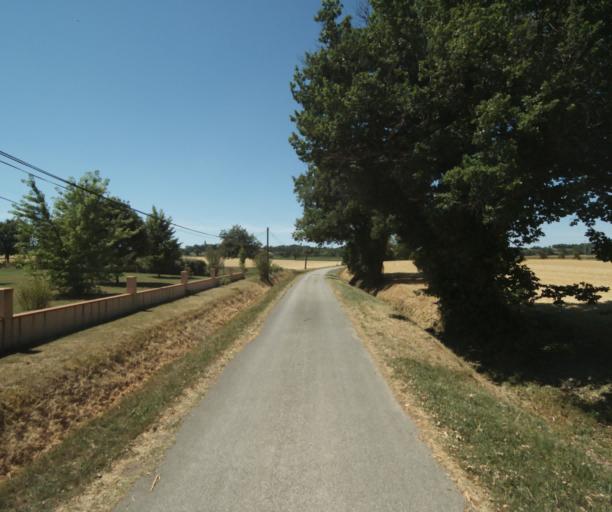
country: FR
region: Midi-Pyrenees
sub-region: Departement de la Haute-Garonne
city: Saint-Felix-Lauragais
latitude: 43.4790
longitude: 1.9388
